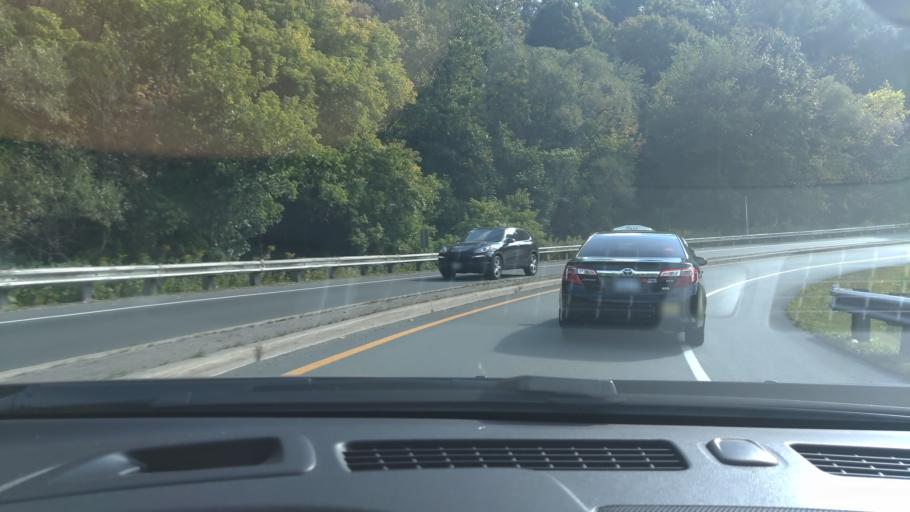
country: CA
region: Ontario
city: Toronto
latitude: 43.6830
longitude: -79.3602
